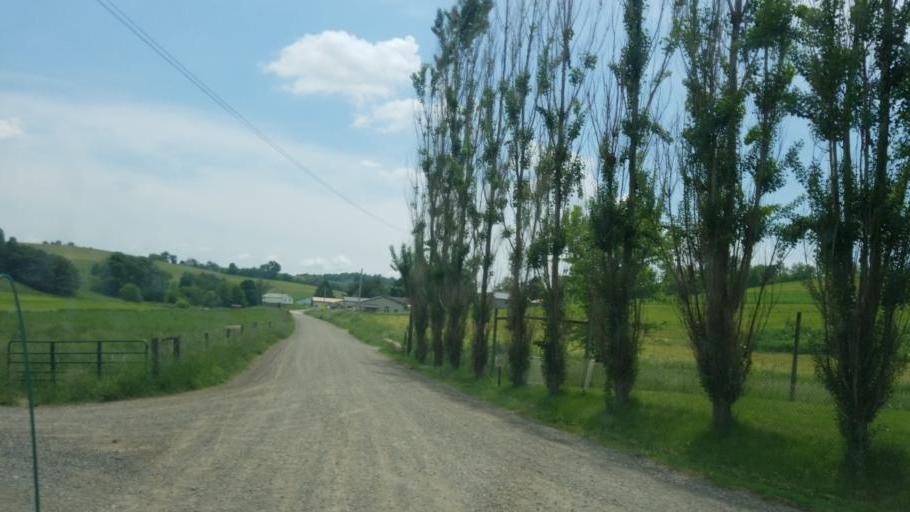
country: US
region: Ohio
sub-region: Holmes County
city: Millersburg
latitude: 40.4639
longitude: -81.7970
